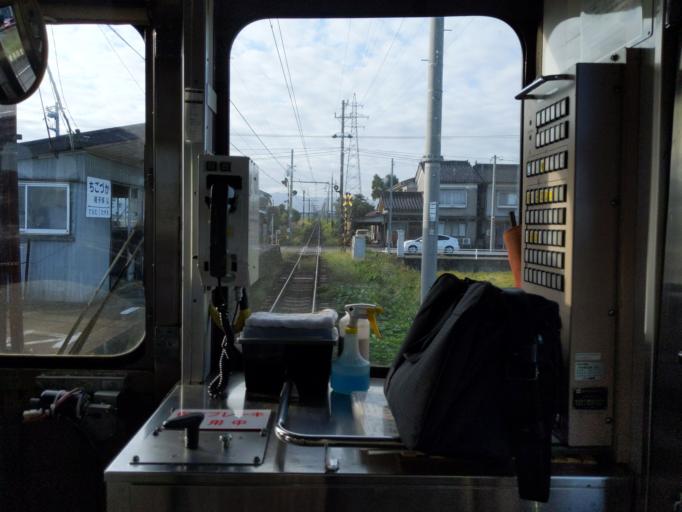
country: JP
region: Toyama
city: Kamiichi
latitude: 36.6883
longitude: 137.3178
